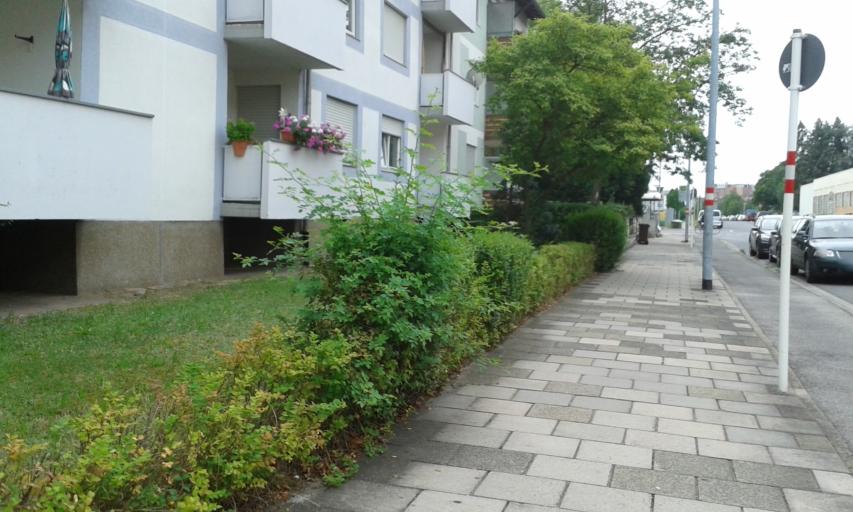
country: DE
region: Bavaria
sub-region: Upper Franconia
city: Bamberg
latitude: 49.8941
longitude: 10.9138
